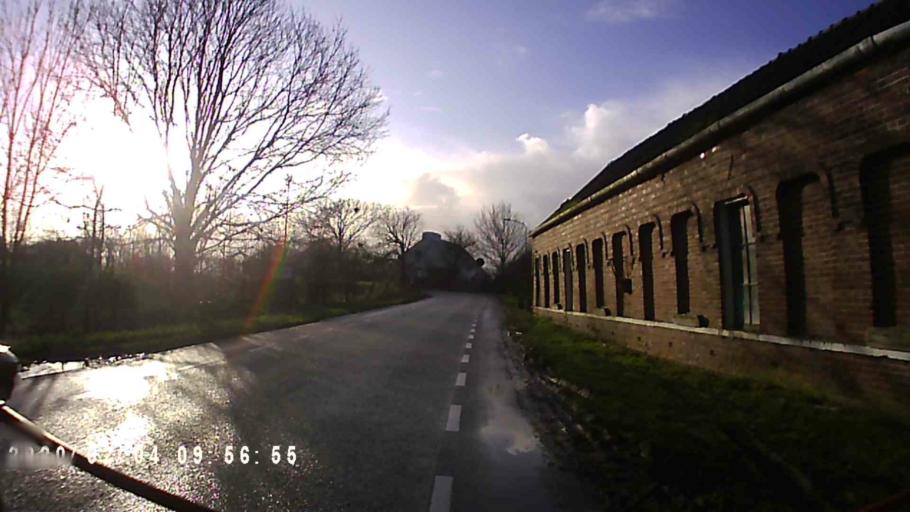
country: NL
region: Groningen
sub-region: Gemeente Zuidhorn
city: Aduard
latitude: 53.2686
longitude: 6.5077
